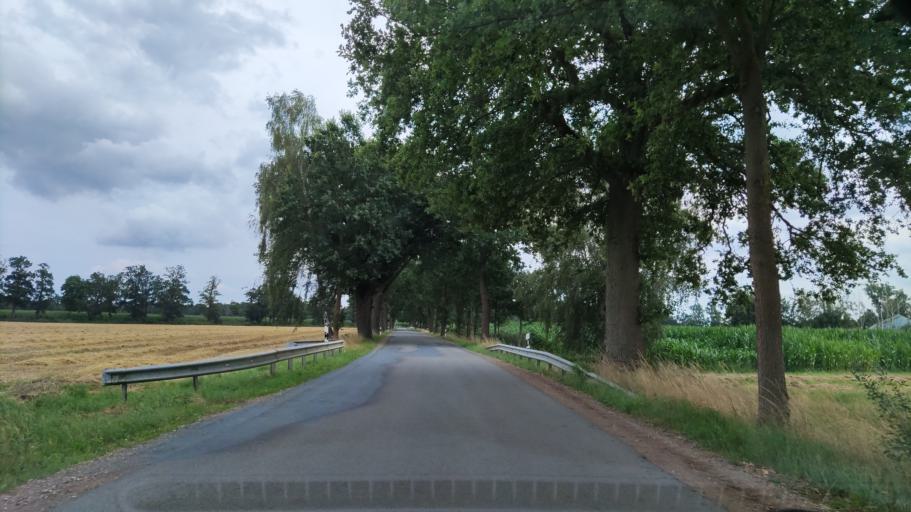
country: DE
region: Lower Saxony
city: Dannenberg
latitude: 53.0697
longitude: 11.1291
